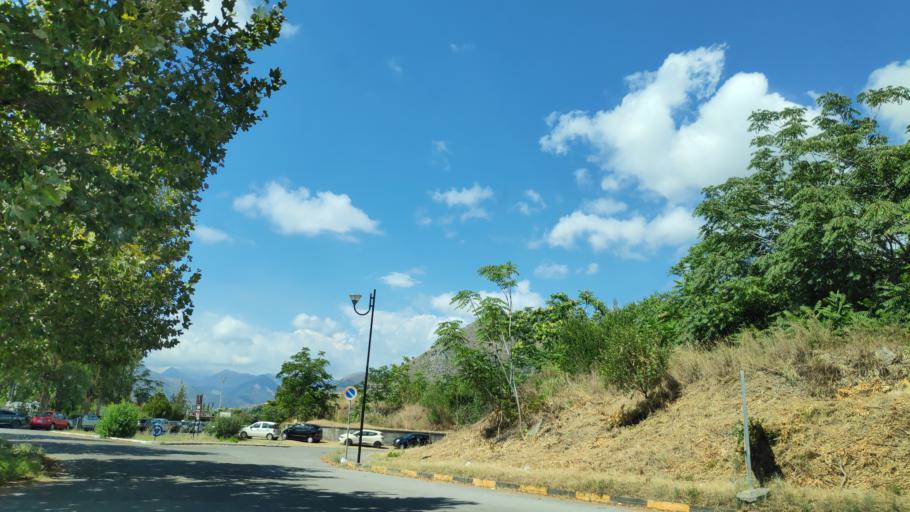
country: IT
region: Calabria
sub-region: Provincia di Cosenza
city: Praia a Mare
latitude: 39.8730
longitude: 15.7873
